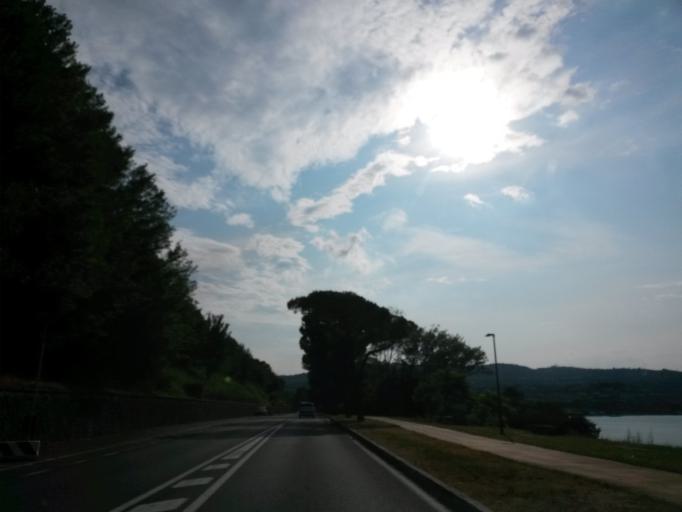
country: IT
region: Lombardy
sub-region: Provincia di Brescia
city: Padenghe sul Garda
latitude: 45.4888
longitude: 10.5293
